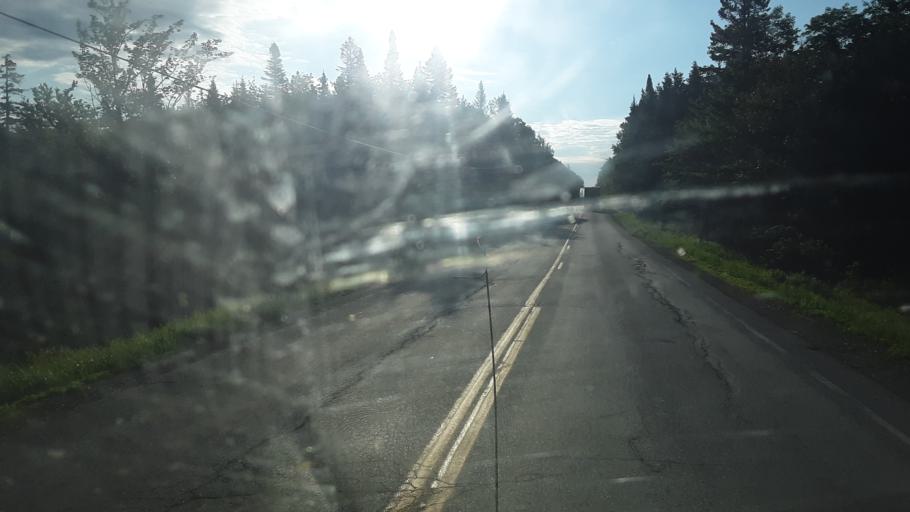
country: US
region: Maine
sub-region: Penobscot County
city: Patten
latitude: 46.2061
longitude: -68.3301
